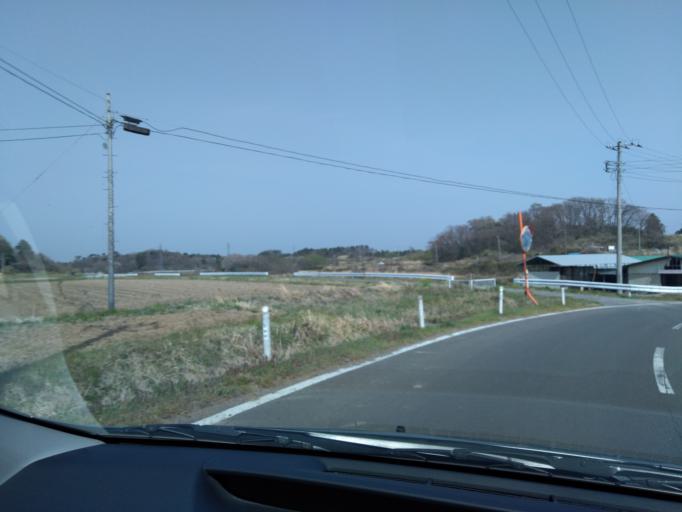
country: JP
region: Miyagi
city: Kogota
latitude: 38.7363
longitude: 141.0733
